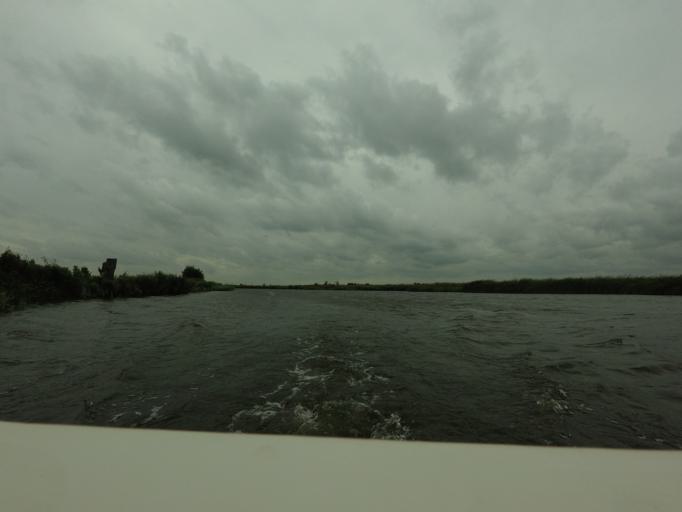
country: NL
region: Friesland
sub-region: Gemeente Boarnsterhim
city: Warten
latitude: 53.1008
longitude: 5.9045
